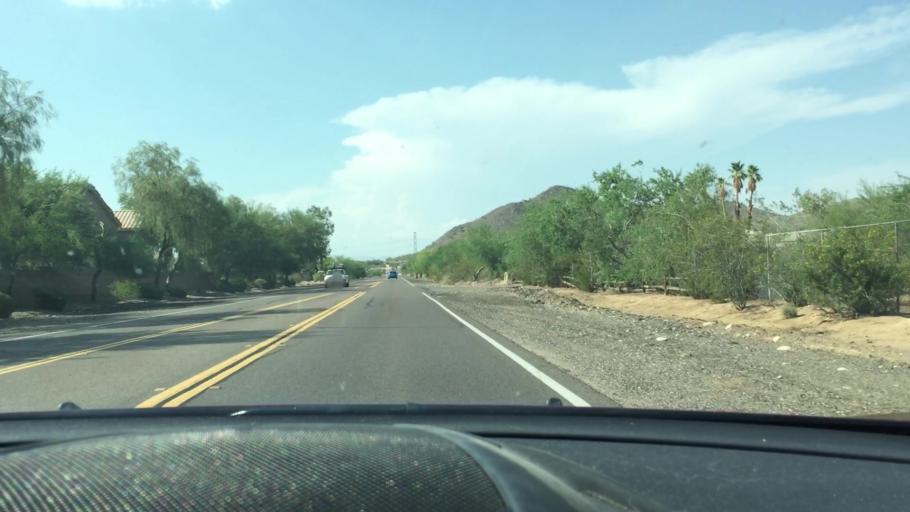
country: US
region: Arizona
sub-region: Maricopa County
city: Sun City West
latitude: 33.7003
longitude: -112.2550
